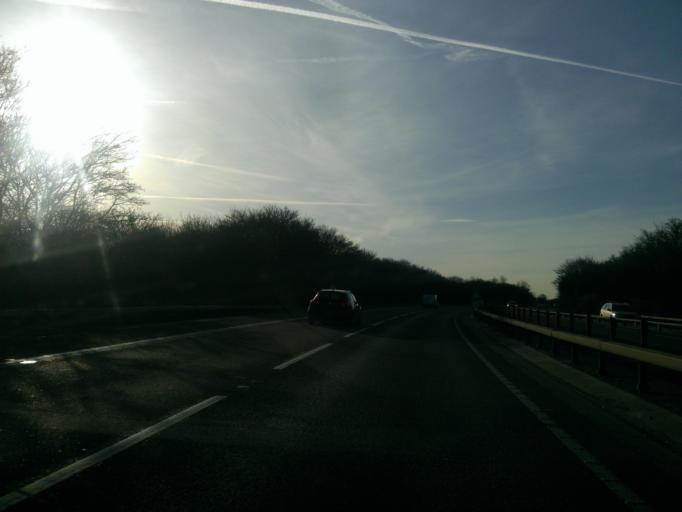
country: GB
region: England
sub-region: Essex
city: Witham
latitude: 51.7956
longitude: 0.6516
